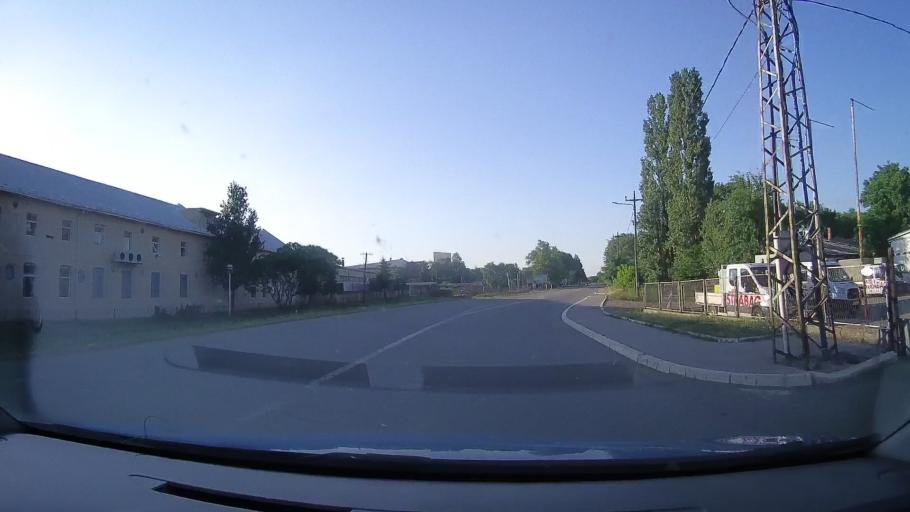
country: RS
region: Autonomna Pokrajina Vojvodina
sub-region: Juznobanatski Okrug
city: Vrsac
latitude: 45.1332
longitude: 21.2868
